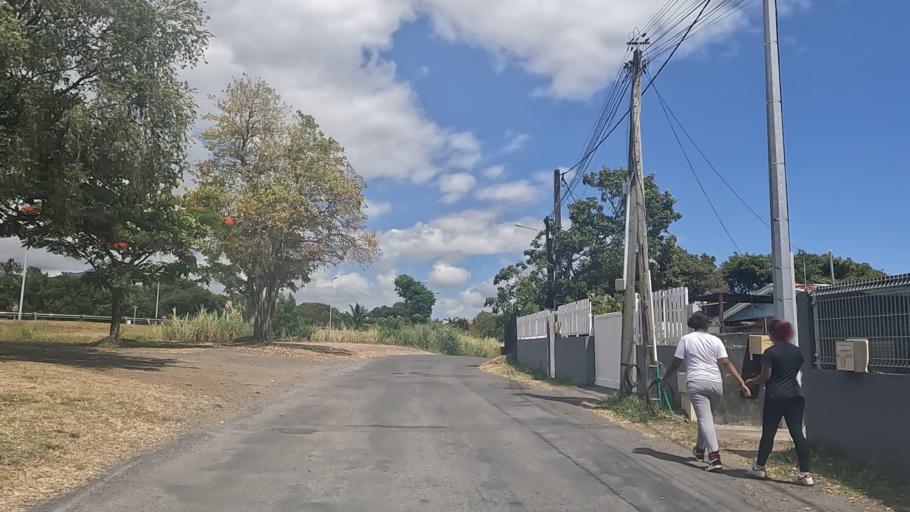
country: RE
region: Reunion
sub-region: Reunion
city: Saint-Benoit
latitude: -21.0339
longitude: 55.7066
